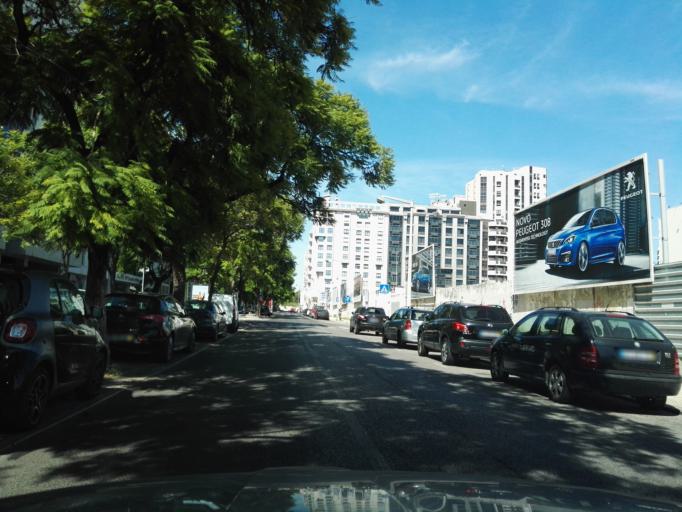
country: PT
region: Lisbon
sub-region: Lisbon
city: Lisbon
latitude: 38.7466
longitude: -9.1499
